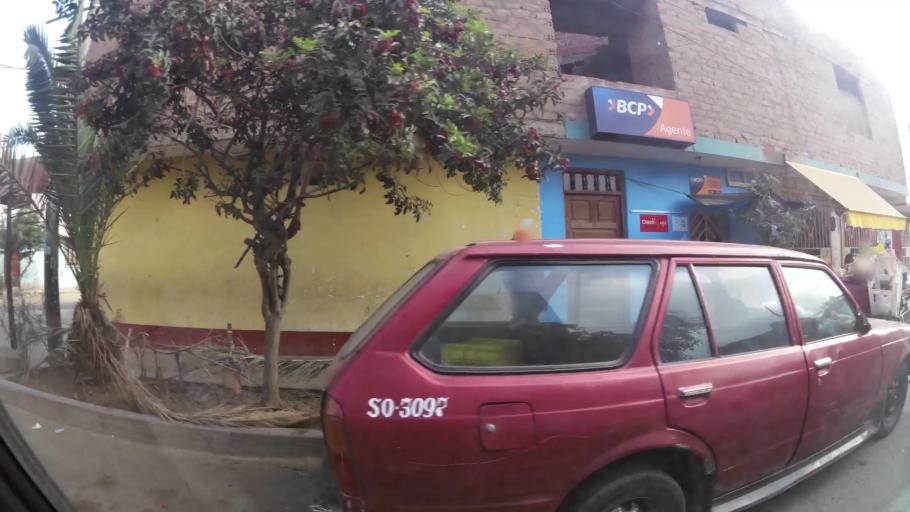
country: PE
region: La Libertad
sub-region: Provincia de Trujillo
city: Trujillo
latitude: -8.1032
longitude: -79.0143
